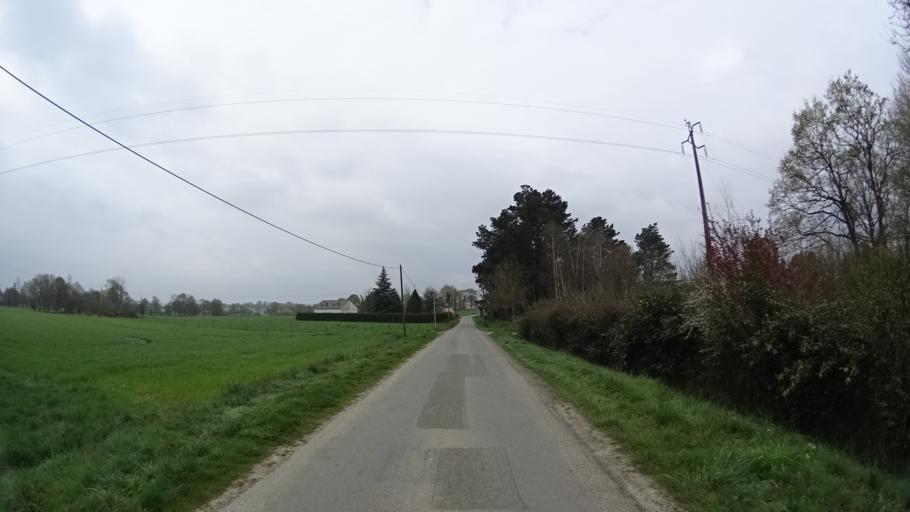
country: FR
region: Brittany
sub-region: Departement d'Ille-et-Vilaine
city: La Chapelle-Thouarault
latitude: 48.1391
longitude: -1.8533
